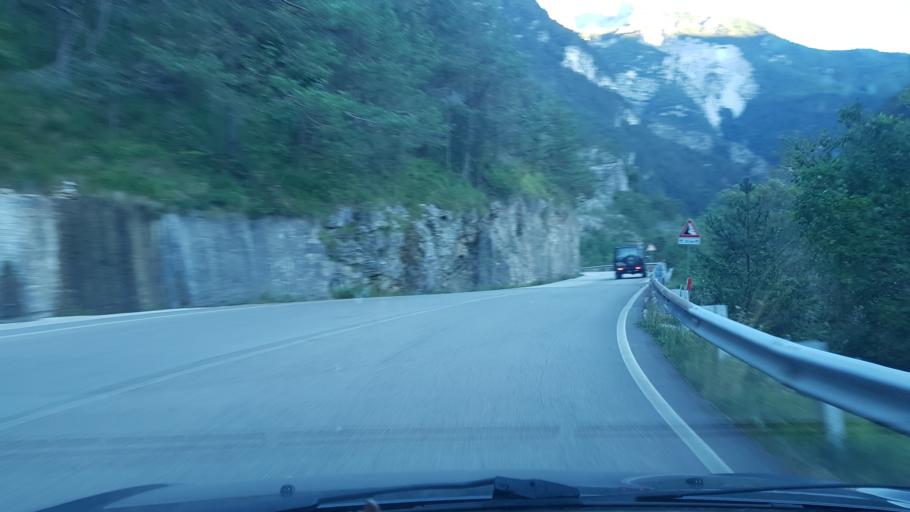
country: IT
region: Veneto
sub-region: Provincia di Belluno
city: Forno di Zoldo
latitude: 46.3389
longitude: 12.2254
